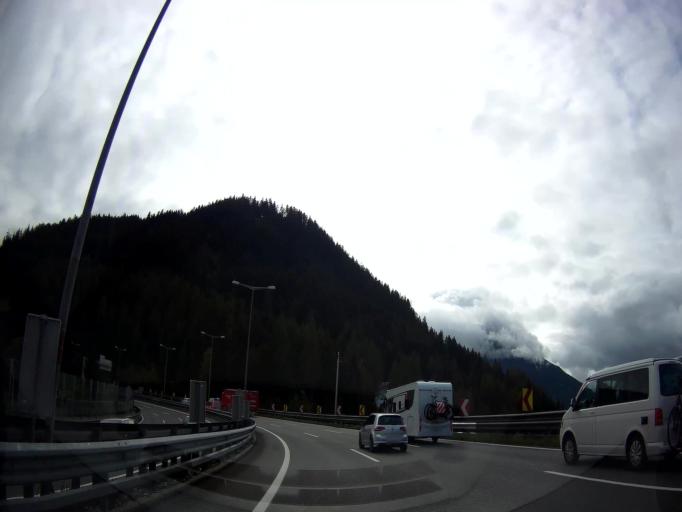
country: AT
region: Tyrol
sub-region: Politischer Bezirk Innsbruck Land
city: Schoenberg im Stubaital
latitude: 47.1825
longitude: 11.3967
